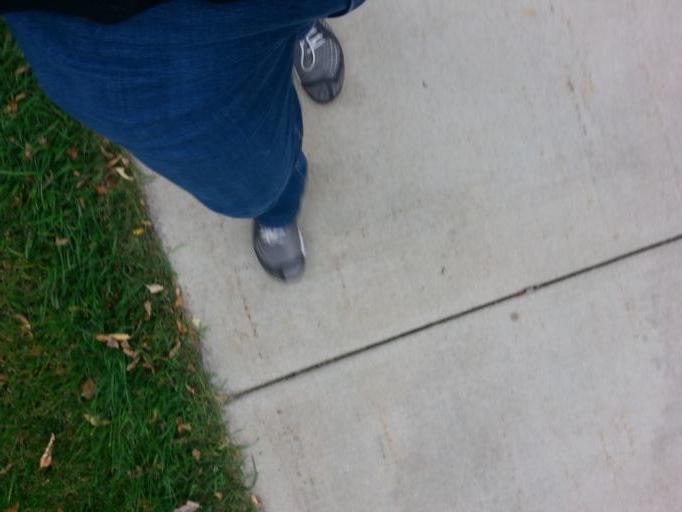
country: US
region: Minnesota
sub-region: Scott County
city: Prior Lake
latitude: 44.7156
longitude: -93.4237
